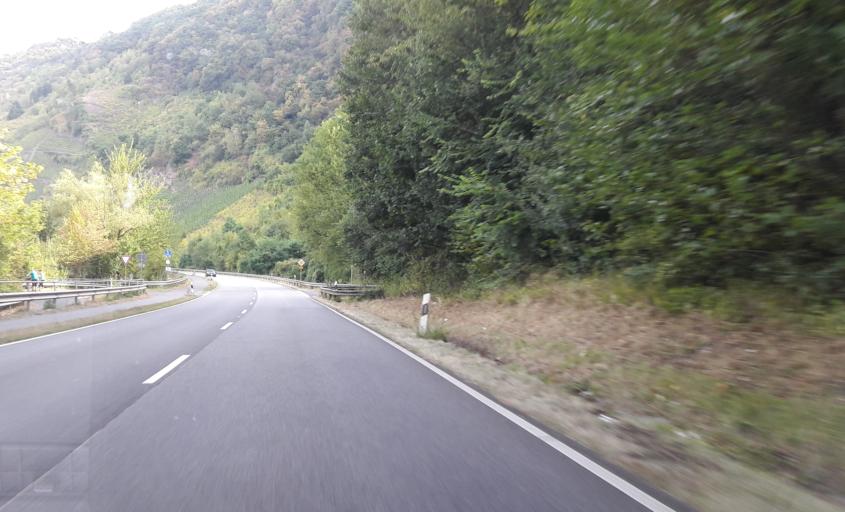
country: DE
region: Rheinland-Pfalz
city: Traben-Trarbach
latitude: 49.9517
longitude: 7.1303
